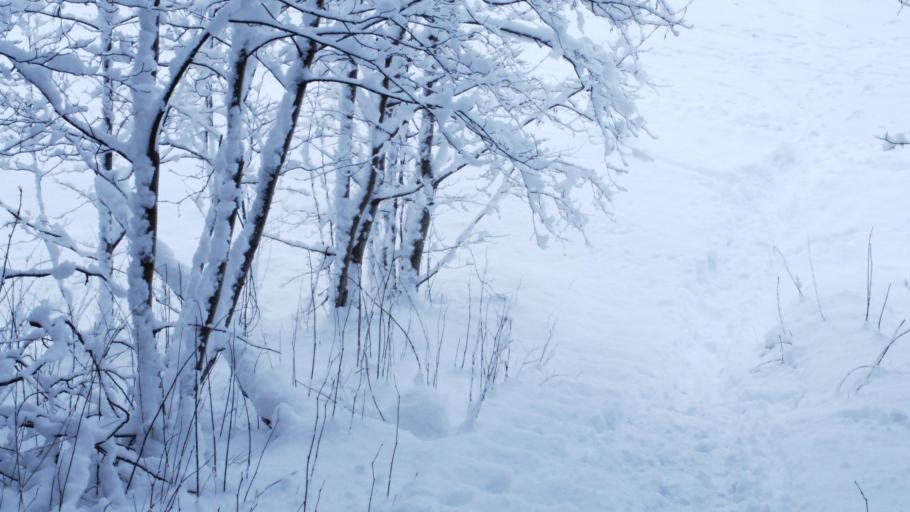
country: NO
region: Nordland
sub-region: Rana
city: Mo i Rana
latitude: 66.3358
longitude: 14.1406
